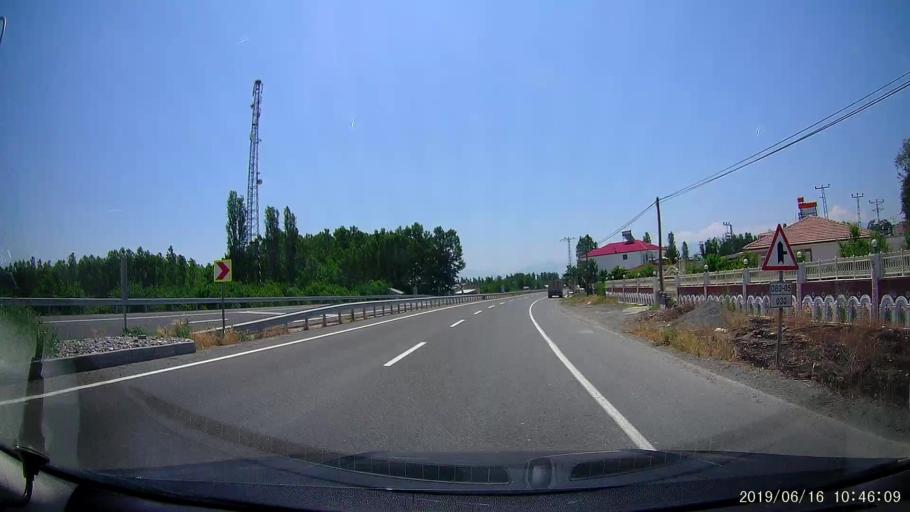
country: AM
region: Armavir
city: Shenavan
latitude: 40.0245
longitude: 43.8773
